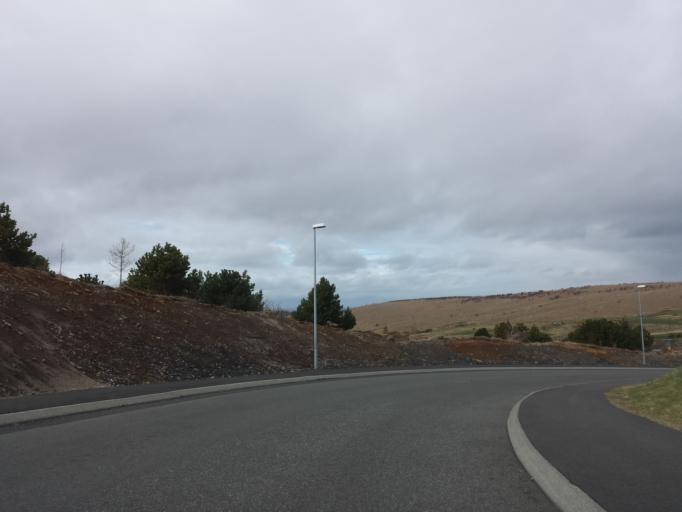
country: IS
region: Capital Region
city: Kopavogur
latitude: 64.0880
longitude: -21.8633
